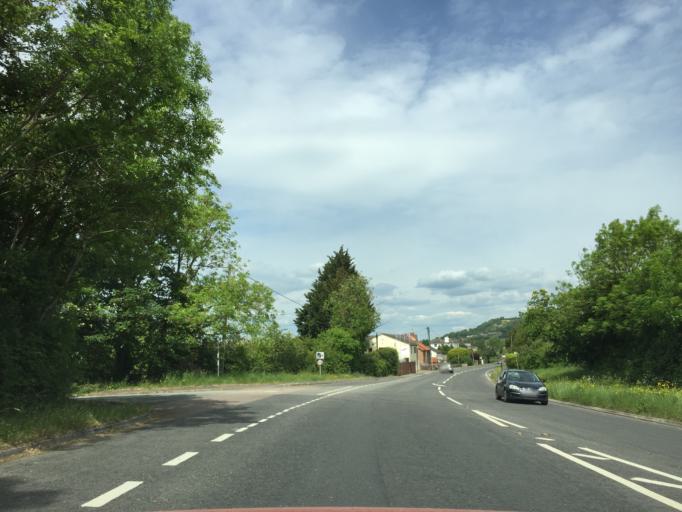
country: GB
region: England
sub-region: Gloucestershire
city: Gloucester
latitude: 51.8124
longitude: -2.2421
